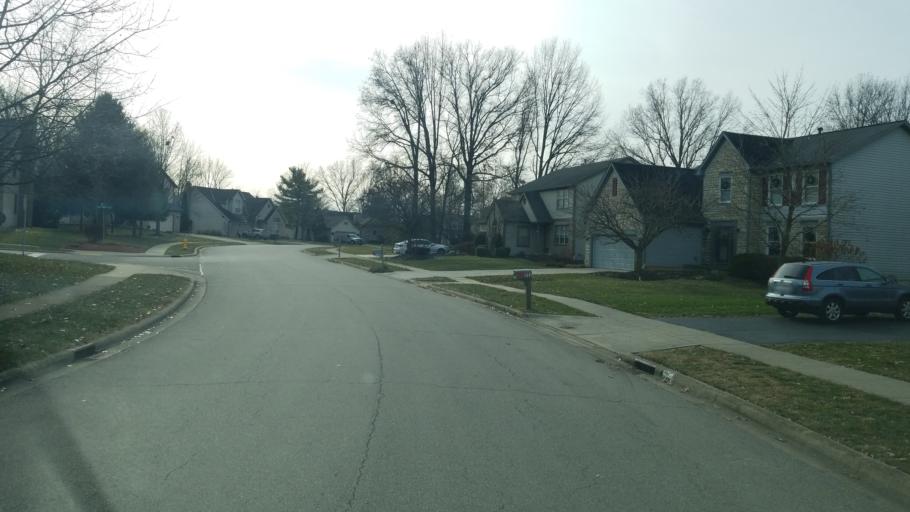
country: US
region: Ohio
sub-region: Delaware County
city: Lewis Center
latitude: 40.1643
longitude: -83.0274
